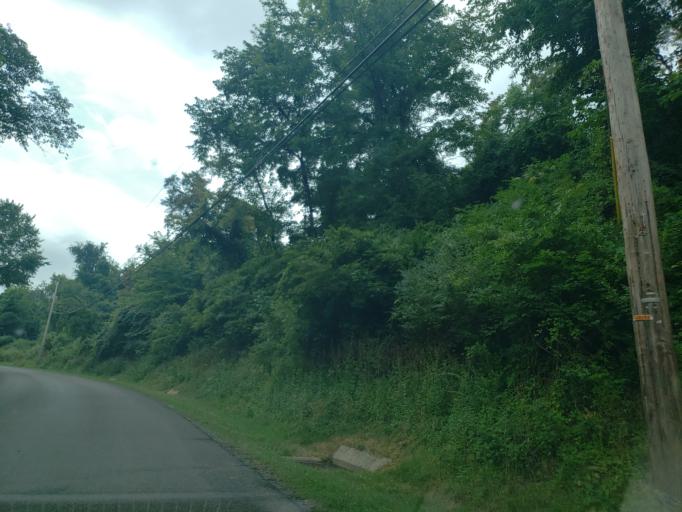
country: US
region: Pennsylvania
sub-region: Allegheny County
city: Emsworth
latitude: 40.5279
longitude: -80.1233
